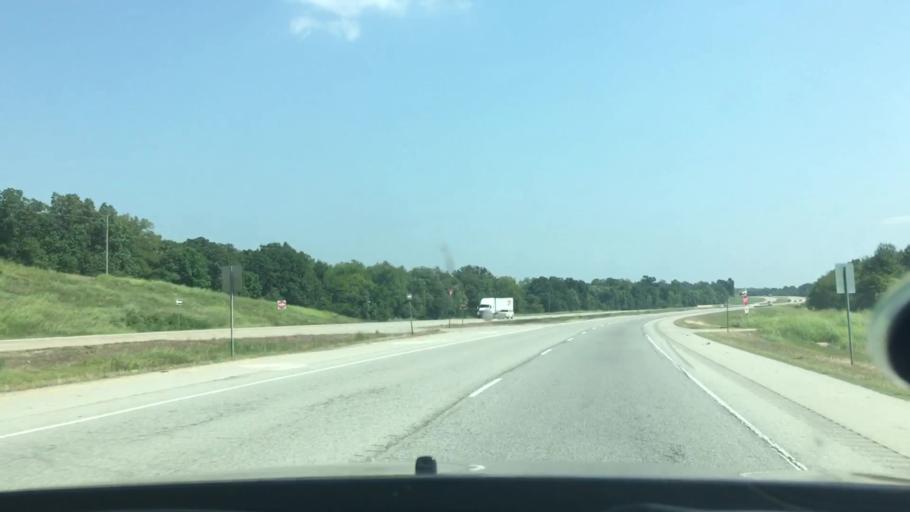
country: US
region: Oklahoma
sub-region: Atoka County
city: Atoka
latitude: 34.2964
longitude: -96.1888
